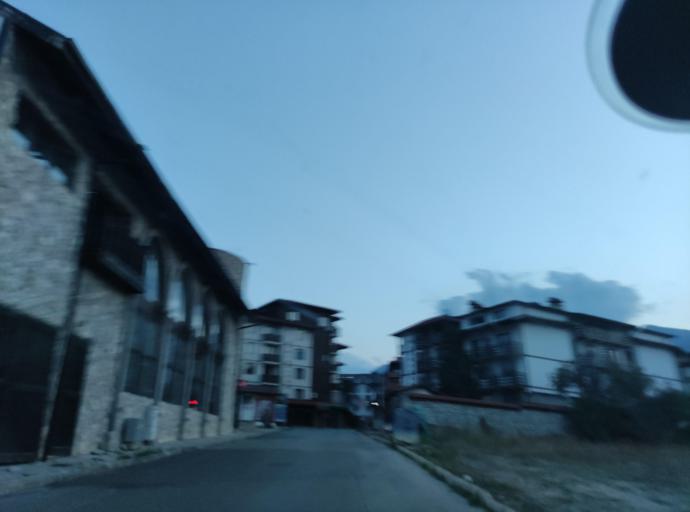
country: BG
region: Blagoevgrad
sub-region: Obshtina Bansko
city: Bansko
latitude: 41.8278
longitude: 23.4827
